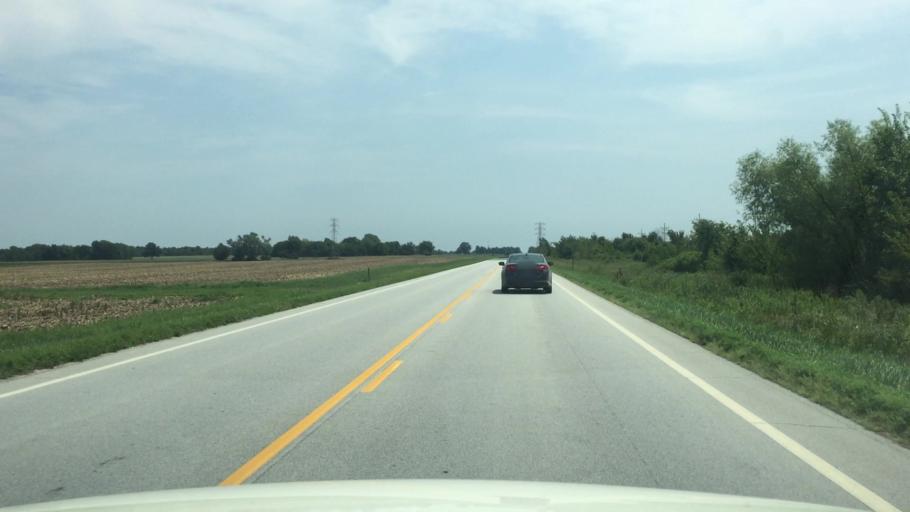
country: US
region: Kansas
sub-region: Cherokee County
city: Columbus
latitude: 37.1791
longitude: -94.9114
